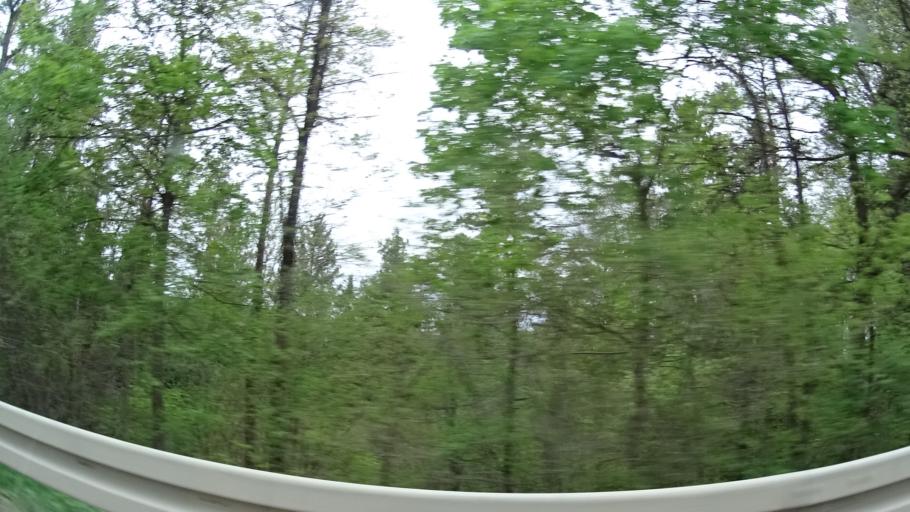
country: DE
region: Baden-Wuerttemberg
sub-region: Freiburg Region
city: Niedereschach
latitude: 48.1535
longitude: 8.5516
